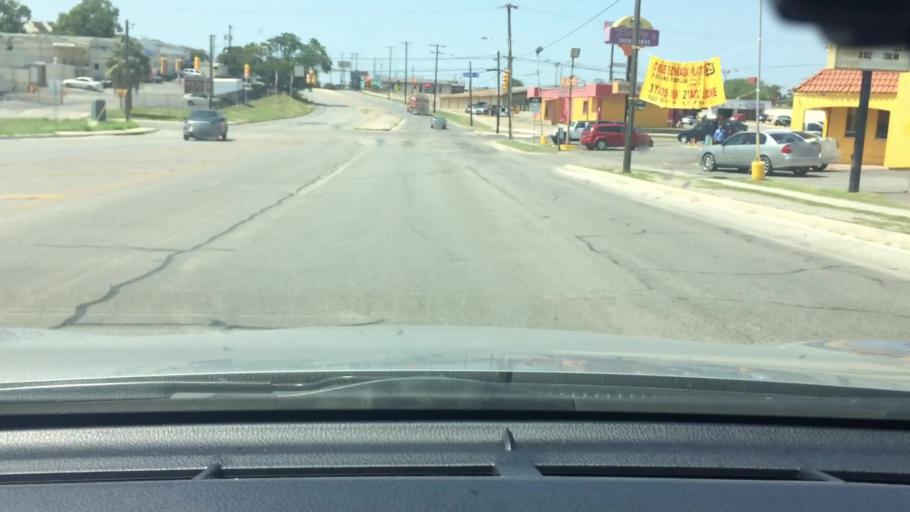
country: US
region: Texas
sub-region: Bexar County
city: San Antonio
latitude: 29.3678
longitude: -98.4377
